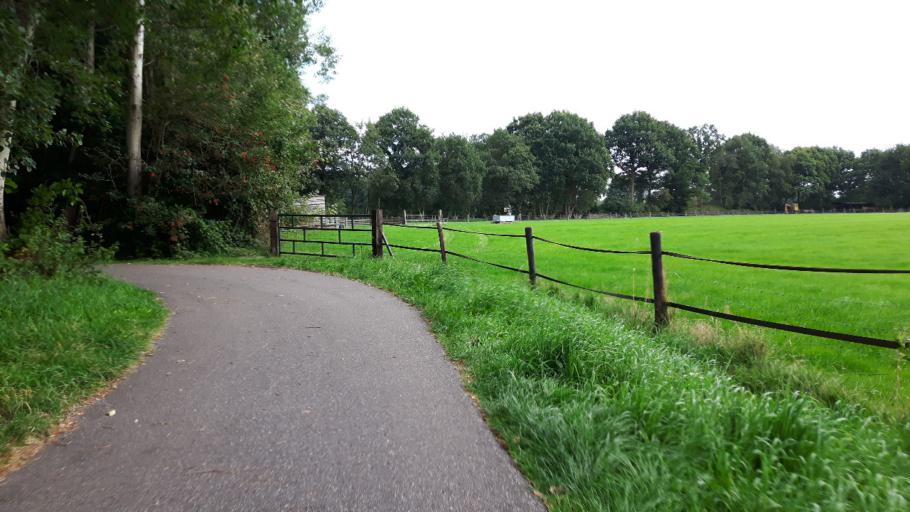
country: NL
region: Groningen
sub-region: Gemeente Leek
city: Leek
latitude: 53.1098
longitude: 6.4353
